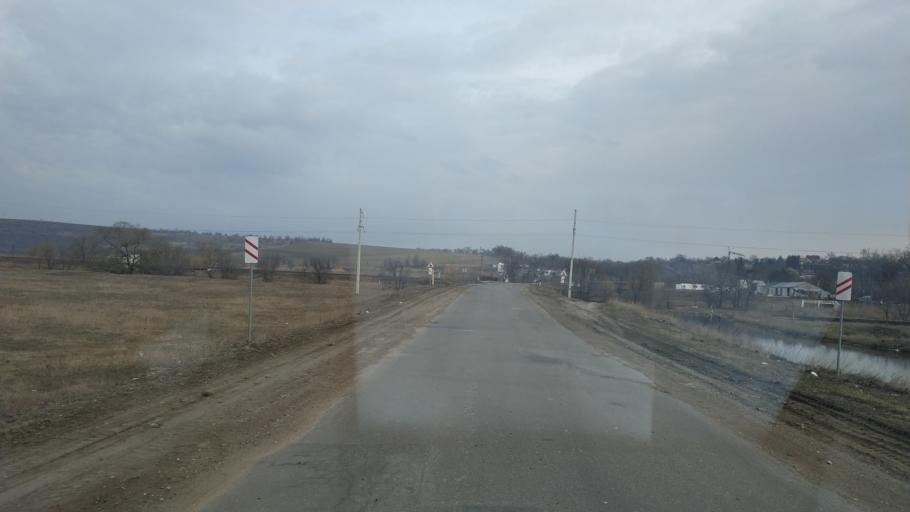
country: MD
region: Chisinau
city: Singera
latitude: 46.9221
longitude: 29.0466
